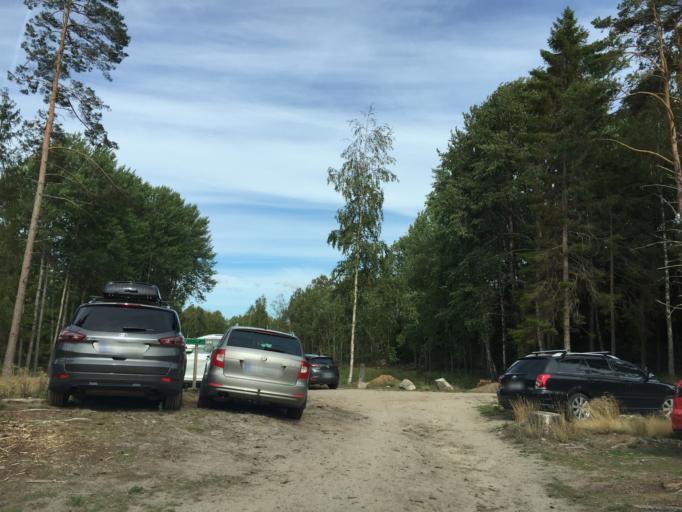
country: NO
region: Ostfold
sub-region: Fredrikstad
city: Fredrikstad
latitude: 59.0979
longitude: 10.9263
